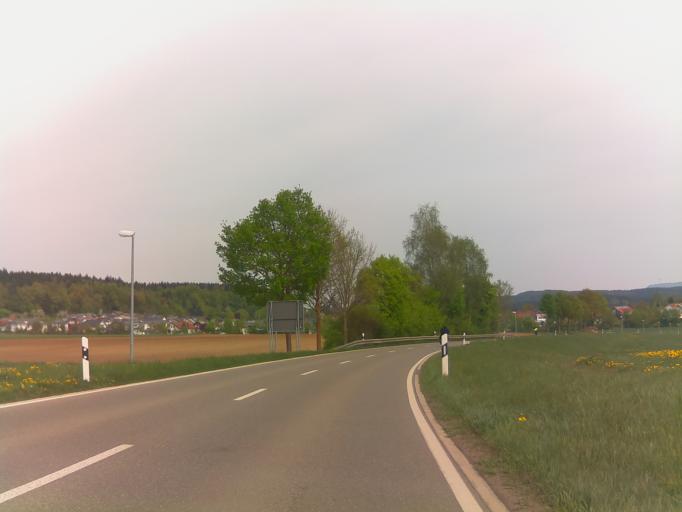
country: DE
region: Baden-Wuerttemberg
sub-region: Freiburg Region
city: Deisslingen
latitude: 48.1193
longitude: 8.6119
